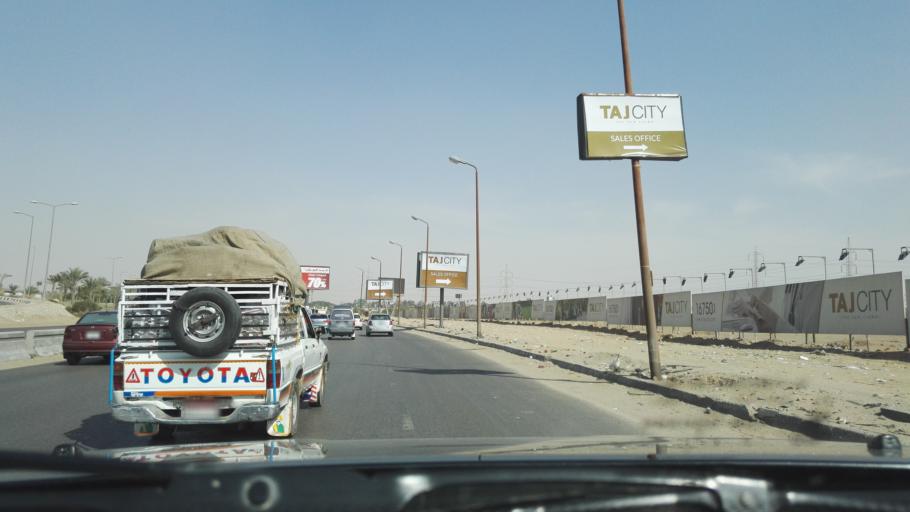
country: EG
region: Muhafazat al Qalyubiyah
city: Al Khankah
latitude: 30.0790
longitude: 31.4226
